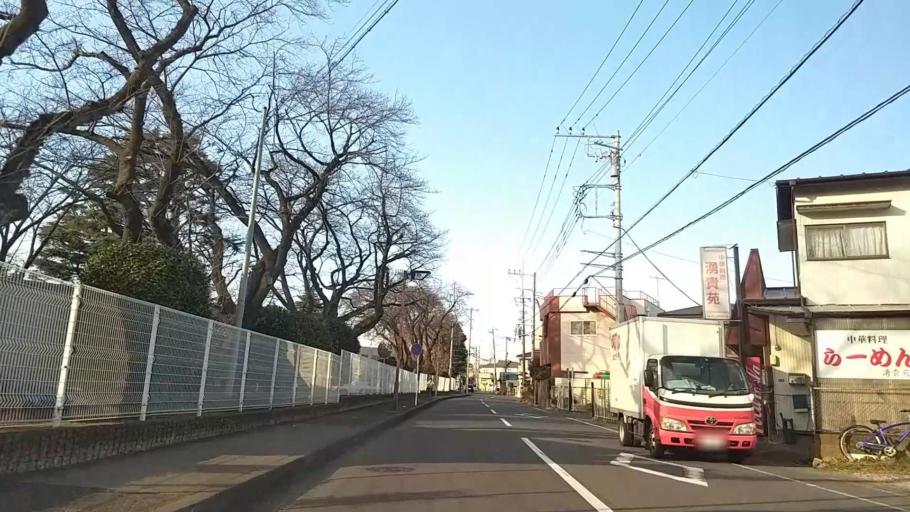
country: JP
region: Kanagawa
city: Atsugi
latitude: 35.4441
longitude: 139.3475
